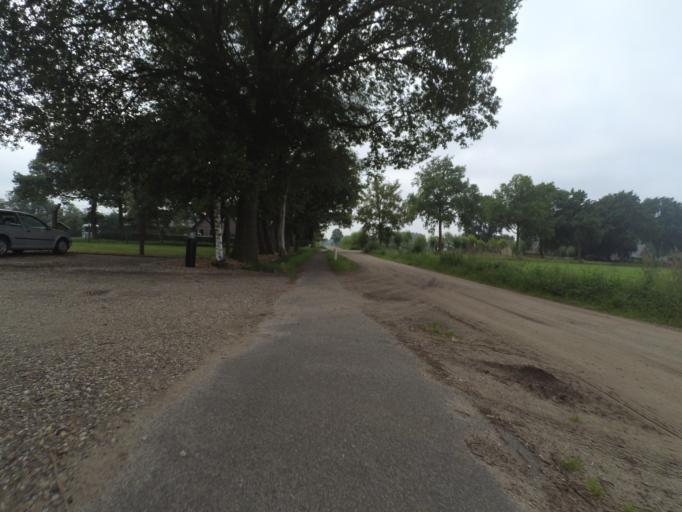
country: NL
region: Gelderland
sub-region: Gemeente Barneveld
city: Kootwijkerbroek
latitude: 52.1215
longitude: 5.6573
